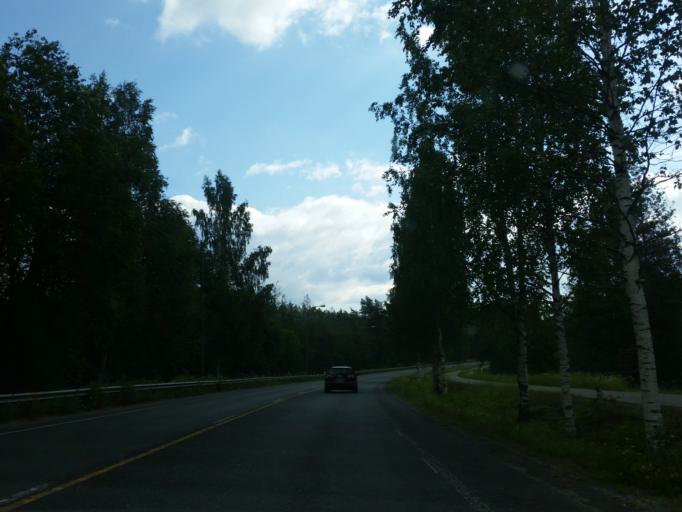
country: FI
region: Northern Savo
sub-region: Kuopio
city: Kuopio
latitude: 62.8401
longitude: 27.5837
